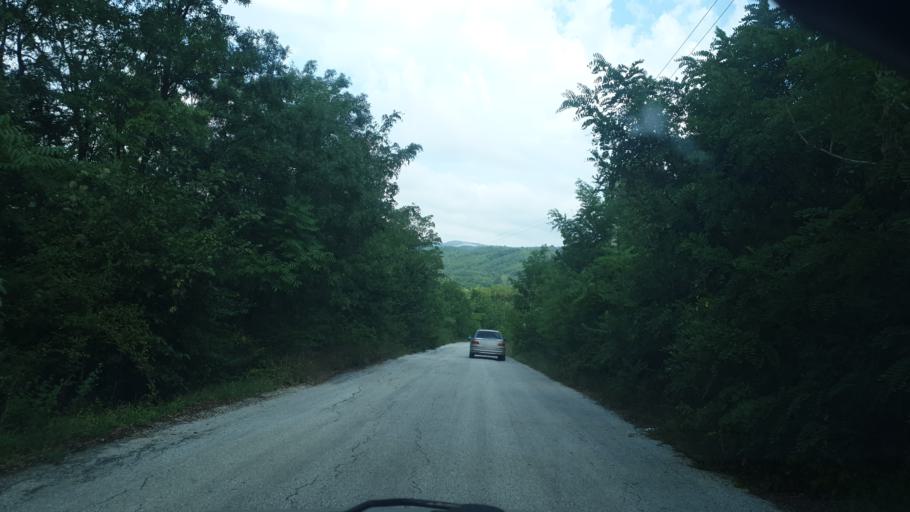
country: RS
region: Central Serbia
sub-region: Sumadijski Okrug
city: Kragujevac
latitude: 44.1039
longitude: 20.7901
